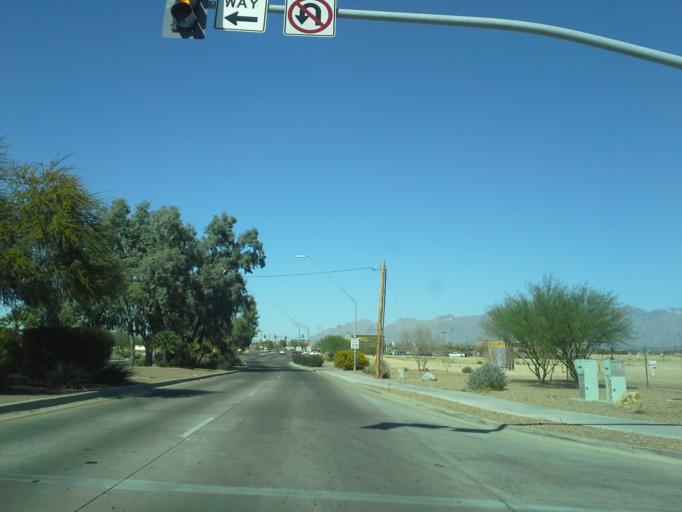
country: US
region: Arizona
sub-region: Pima County
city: South Tucson
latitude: 32.1851
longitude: -110.9561
